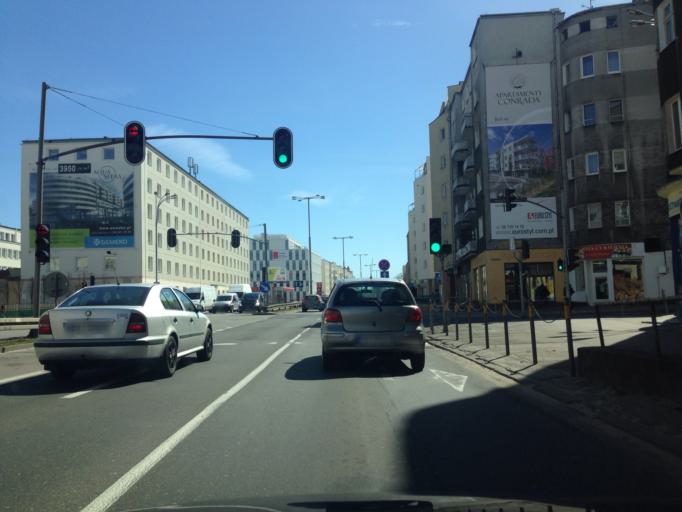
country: PL
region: Pomeranian Voivodeship
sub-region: Gdynia
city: Gdynia
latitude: 54.5150
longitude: 18.5324
